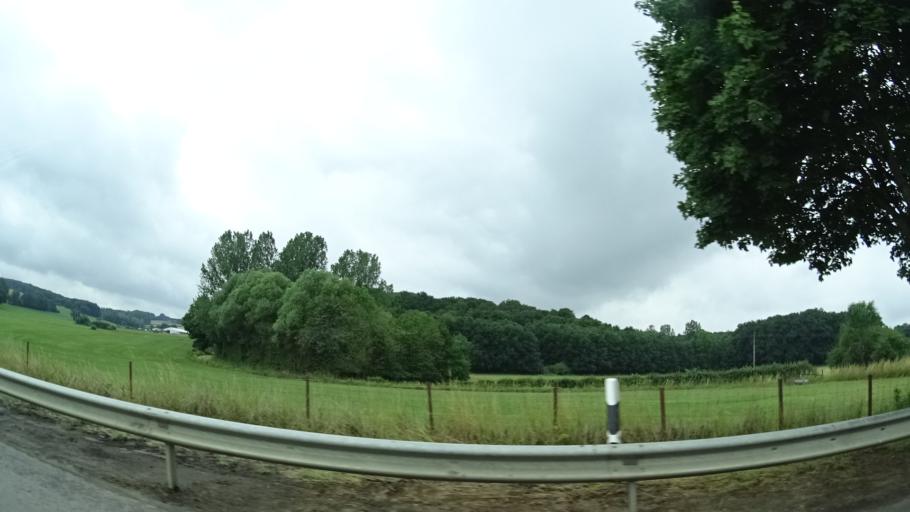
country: LU
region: Luxembourg
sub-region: Canton de Capellen
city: Garnich
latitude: 49.6345
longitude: 5.9556
